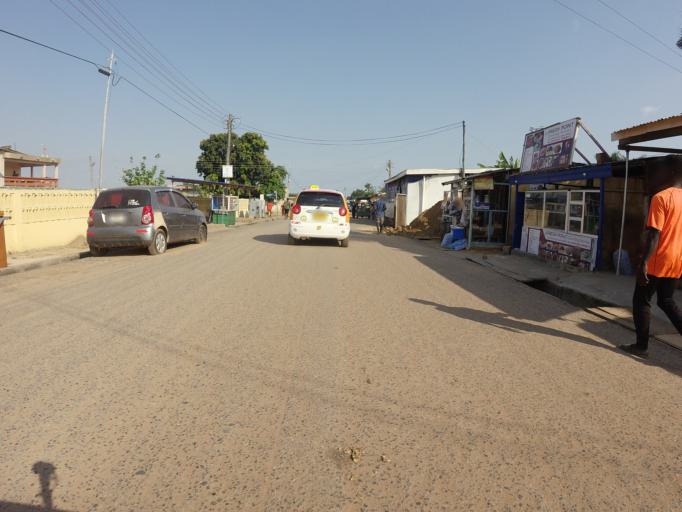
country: GH
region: Greater Accra
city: Dome
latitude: 5.6135
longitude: -0.2357
